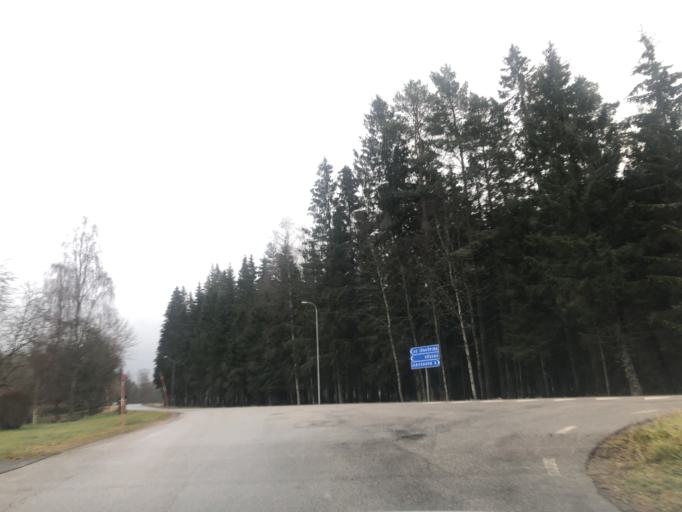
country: SE
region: Vaestra Goetaland
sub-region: Ulricehamns Kommun
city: Ulricehamn
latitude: 57.8250
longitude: 13.5163
